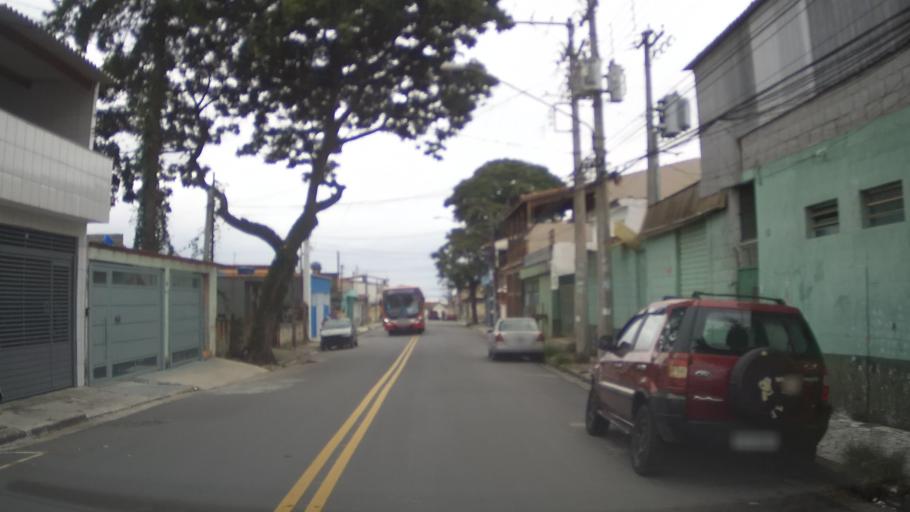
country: BR
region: Sao Paulo
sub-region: Guarulhos
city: Guarulhos
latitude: -23.4470
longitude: -46.5061
